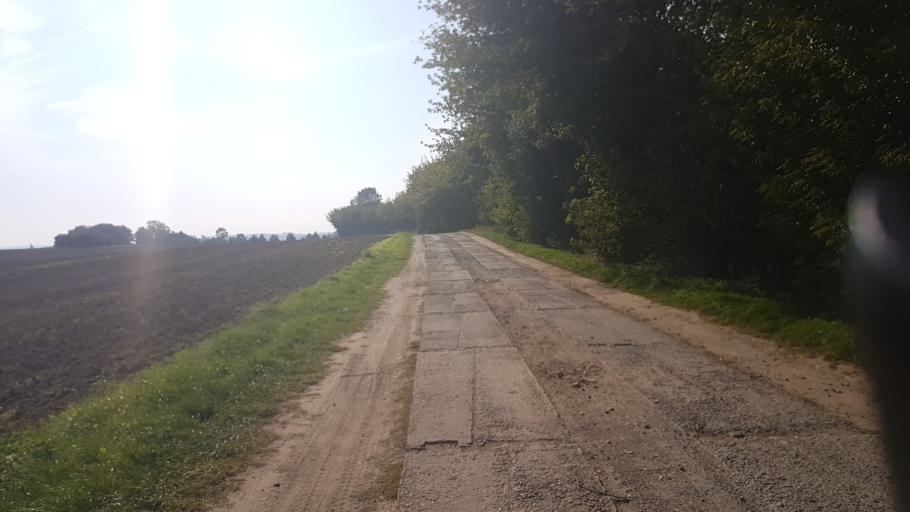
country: DE
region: Mecklenburg-Vorpommern
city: Putbus
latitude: 54.3201
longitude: 13.4426
